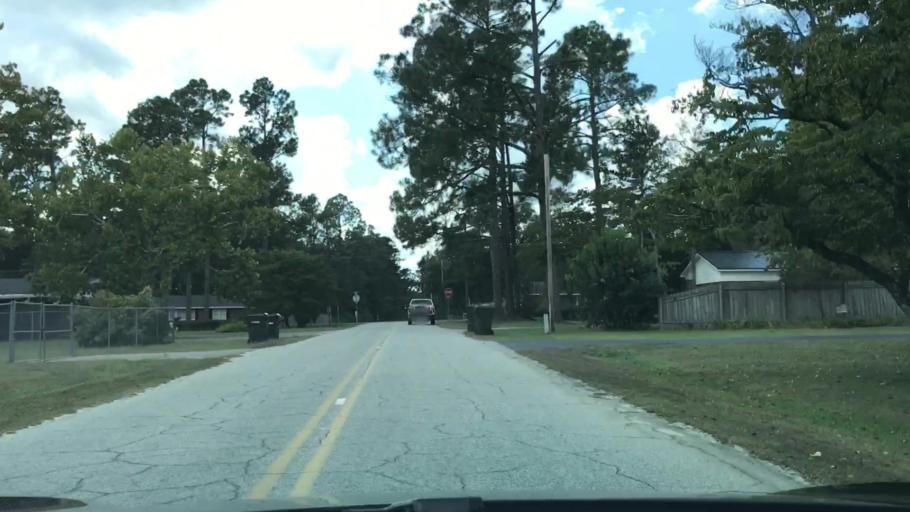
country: US
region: Georgia
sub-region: Jefferson County
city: Wadley
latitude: 32.8711
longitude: -82.3997
